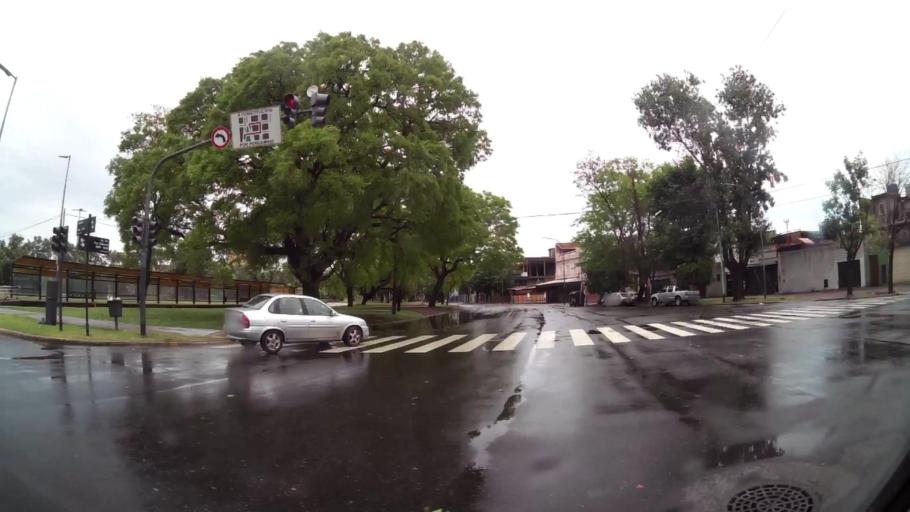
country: AR
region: Buenos Aires F.D.
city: Villa Lugano
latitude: -34.6636
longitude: -58.4378
